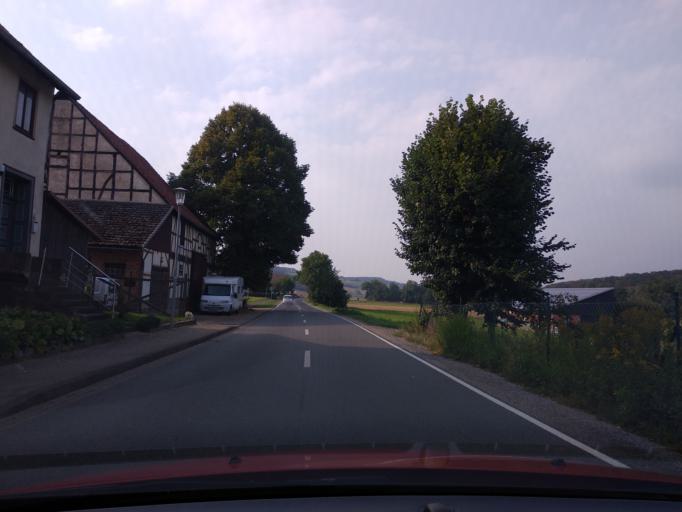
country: DE
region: Hesse
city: Liebenau
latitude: 51.4608
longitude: 9.3066
